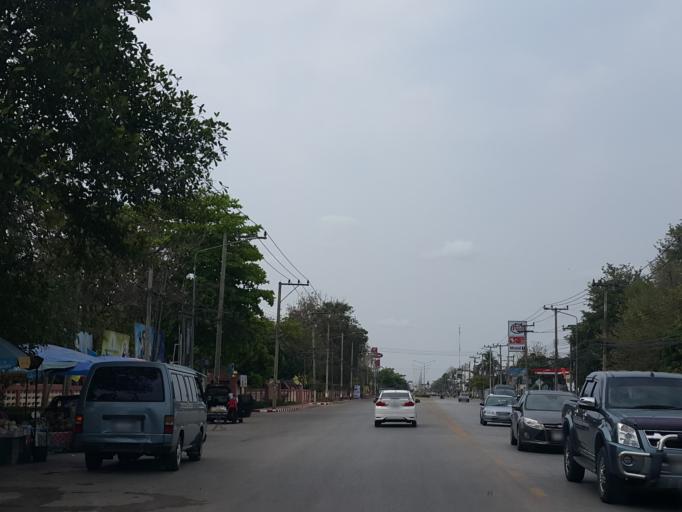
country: TH
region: Lampang
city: Lampang
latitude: 18.2772
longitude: 99.4761
